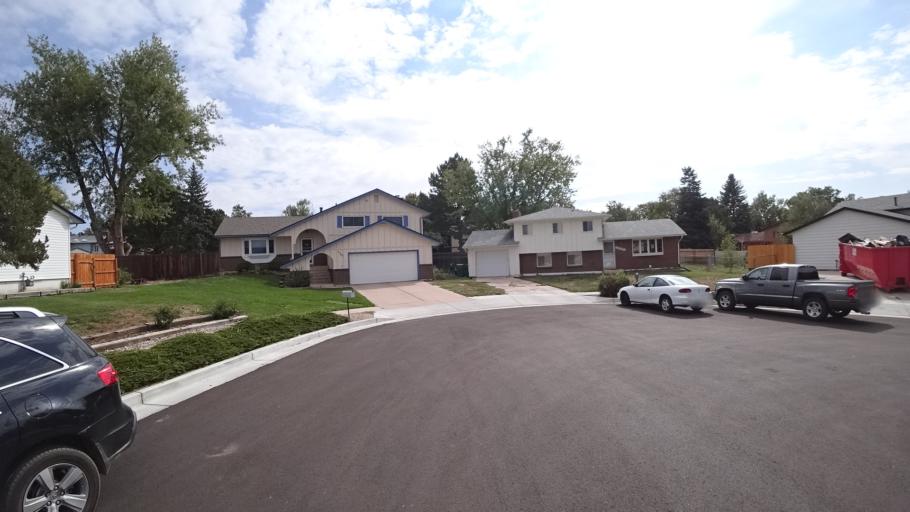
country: US
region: Colorado
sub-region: El Paso County
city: Cimarron Hills
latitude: 38.8535
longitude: -104.7293
